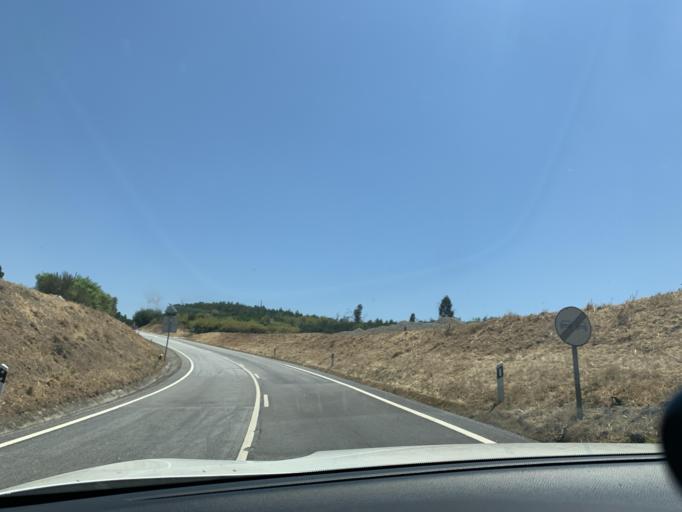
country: PT
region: Viseu
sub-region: Mangualde
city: Mangualde
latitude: 40.5713
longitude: -7.7299
